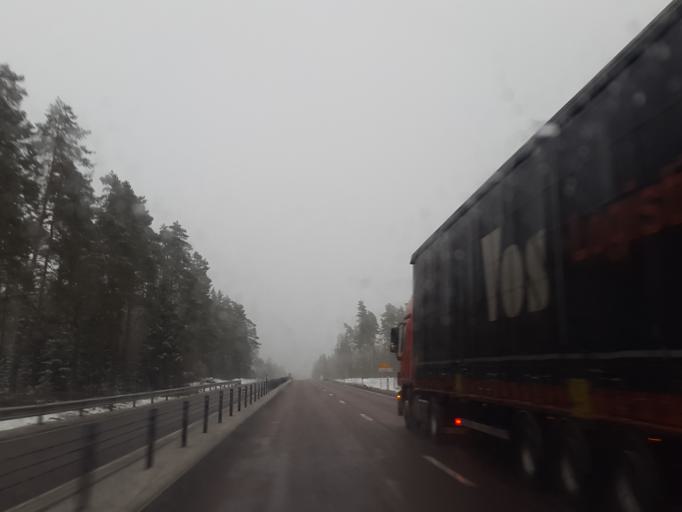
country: SE
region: Joenkoeping
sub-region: Mullsjo Kommun
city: Mullsjoe
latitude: 57.7546
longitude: 13.9171
